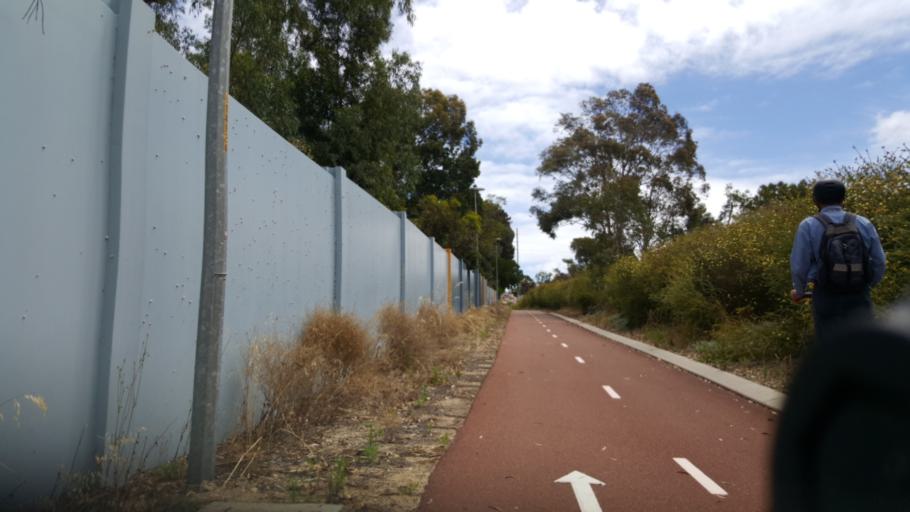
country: AU
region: Western Australia
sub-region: Stirling
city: Westminster
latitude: -31.8687
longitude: 115.8809
